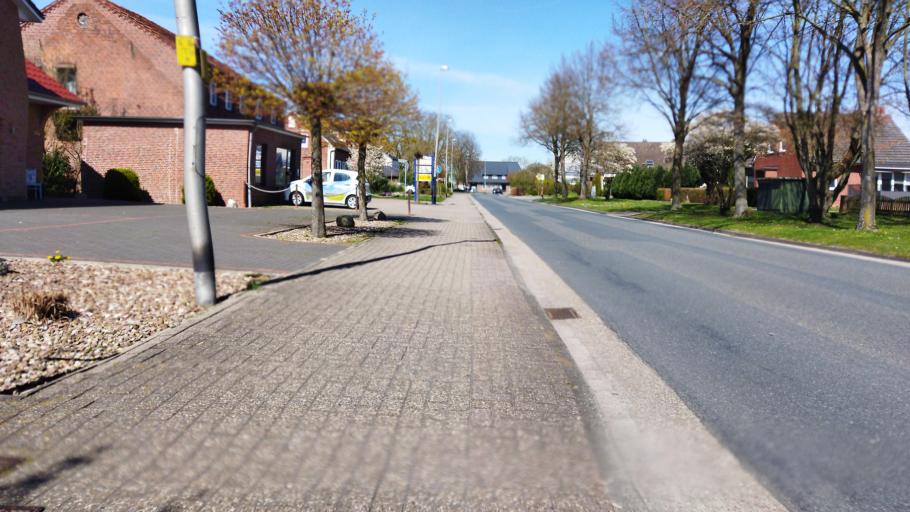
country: DE
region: Lower Saxony
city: Brake (Unterweser)
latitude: 53.3505
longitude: 8.4669
